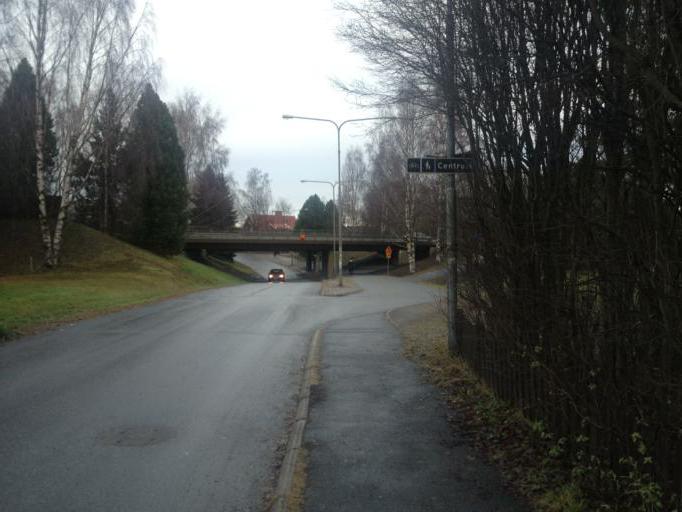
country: SE
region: Vaesterbotten
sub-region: Umea Kommun
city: Umea
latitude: 63.8183
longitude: 20.2643
